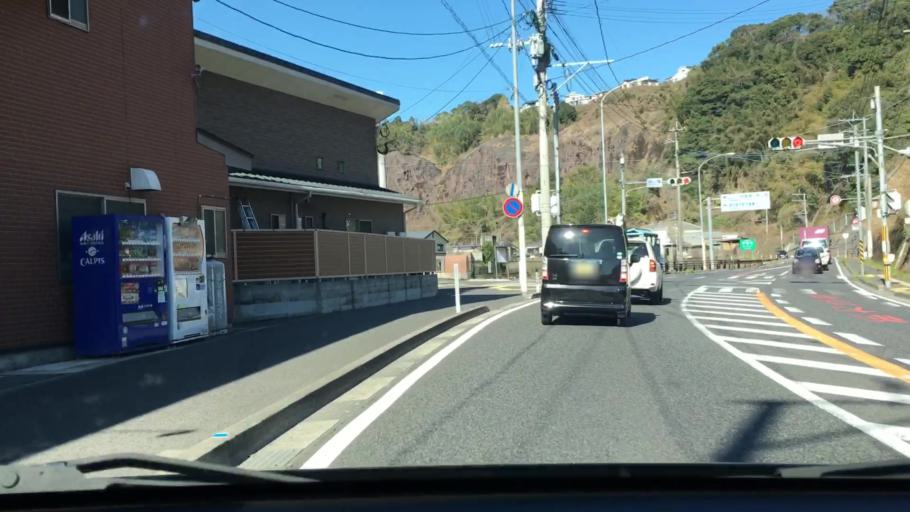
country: JP
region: Kagoshima
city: Kagoshima-shi
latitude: 31.6315
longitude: 130.5240
